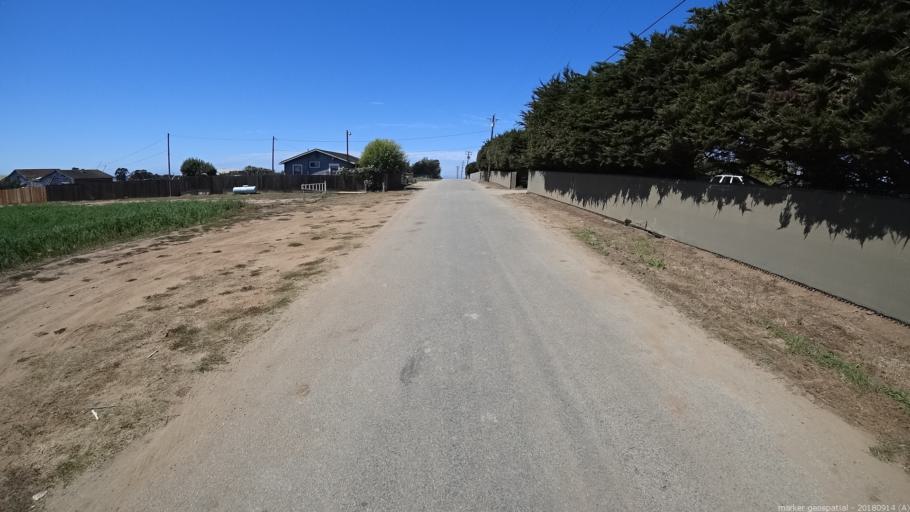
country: US
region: California
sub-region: Monterey County
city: Las Lomas
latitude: 36.8566
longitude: -121.7972
